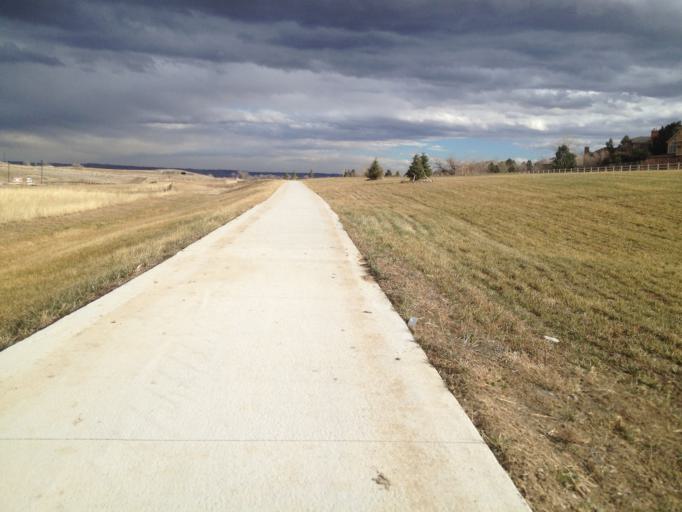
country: US
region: Colorado
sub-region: Boulder County
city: Superior
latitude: 39.9474
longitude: -105.1604
